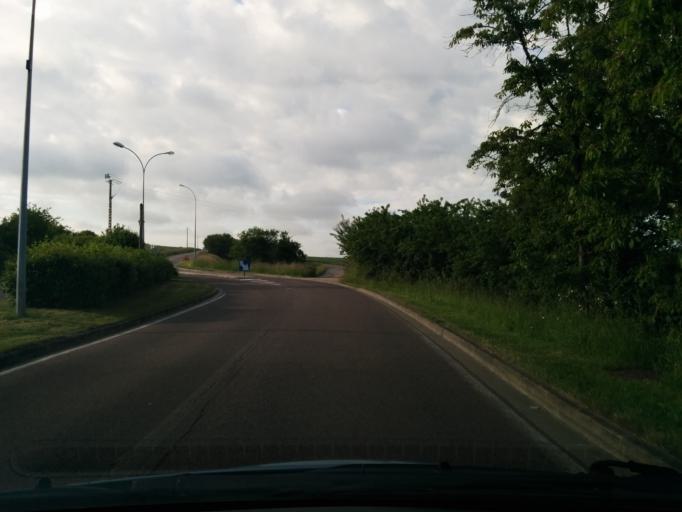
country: FR
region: Ile-de-France
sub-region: Departement des Yvelines
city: Follainville-Dennemont
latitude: 49.0383
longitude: 1.6897
